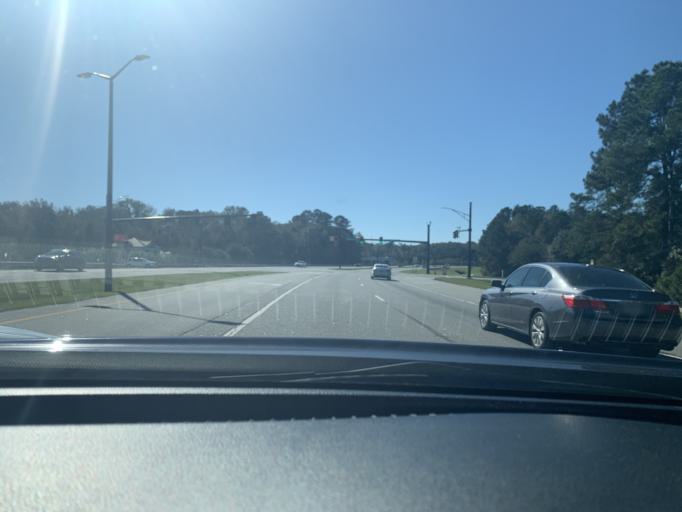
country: US
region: Georgia
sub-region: Chatham County
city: Pooler
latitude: 32.1309
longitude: -81.2570
